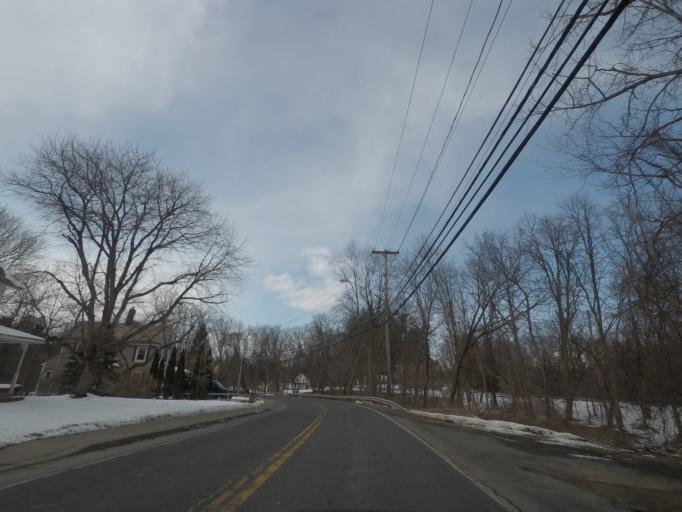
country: US
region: New York
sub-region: Albany County
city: Delmar
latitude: 42.6276
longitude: -73.8568
